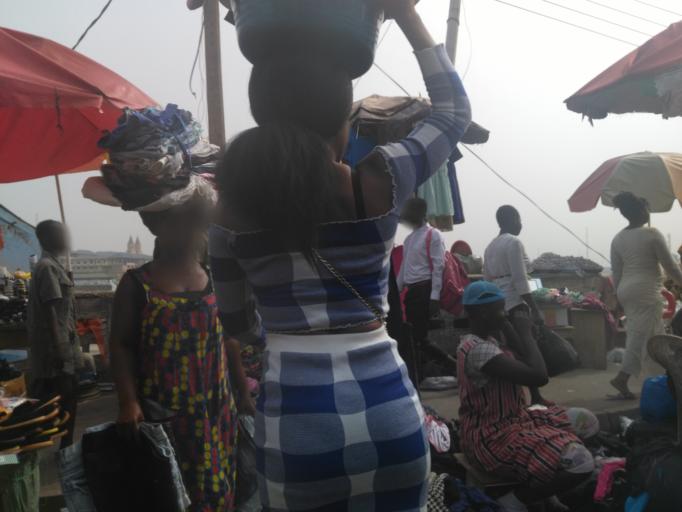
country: GH
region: Ashanti
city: Kumasi
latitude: 6.6987
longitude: -1.6207
